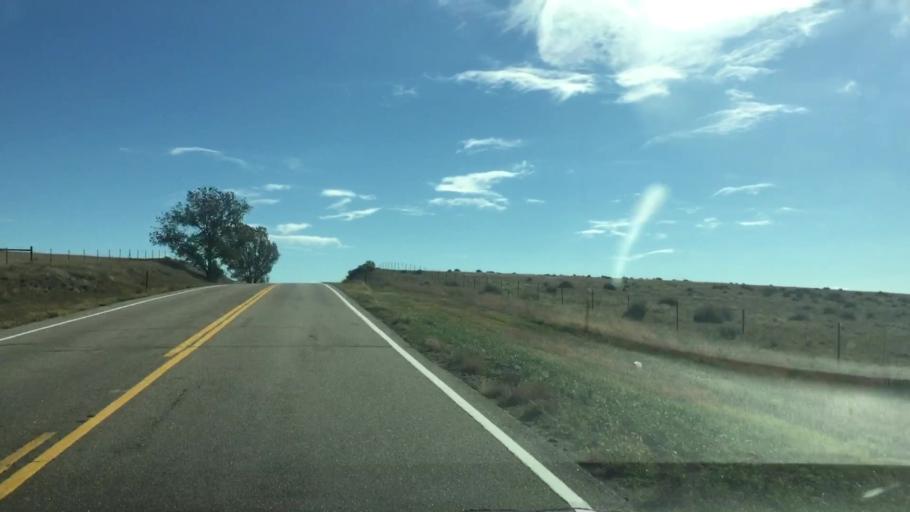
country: US
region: Colorado
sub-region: Elbert County
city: Kiowa
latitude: 39.2736
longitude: -104.2116
